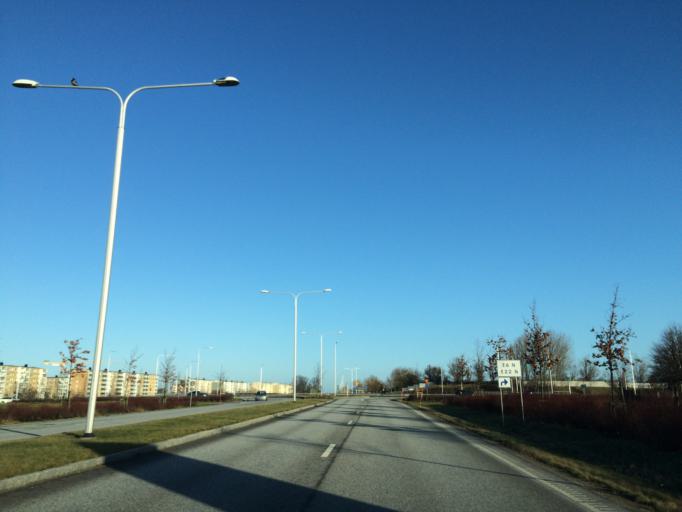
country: SE
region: Skane
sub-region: Malmo
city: Malmoe
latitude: 55.5665
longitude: 12.9859
